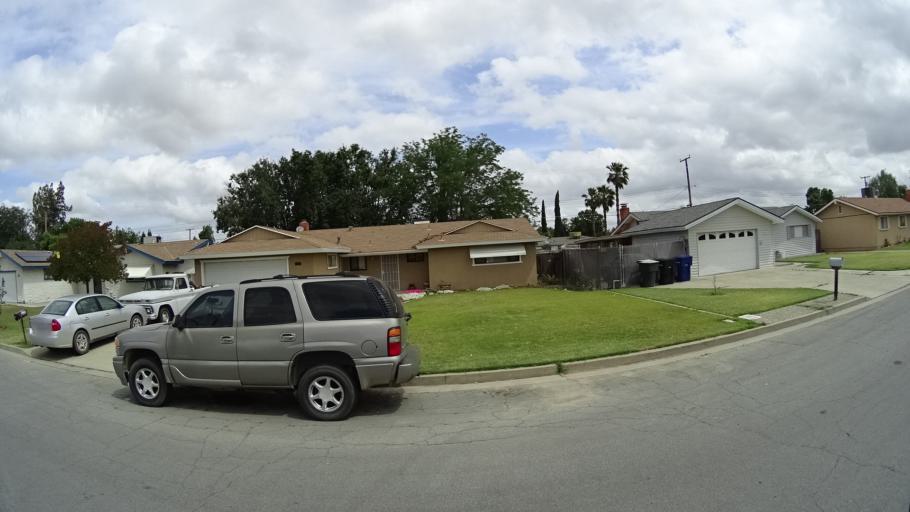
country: US
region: California
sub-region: Kings County
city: Home Garden
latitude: 36.3039
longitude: -119.6574
